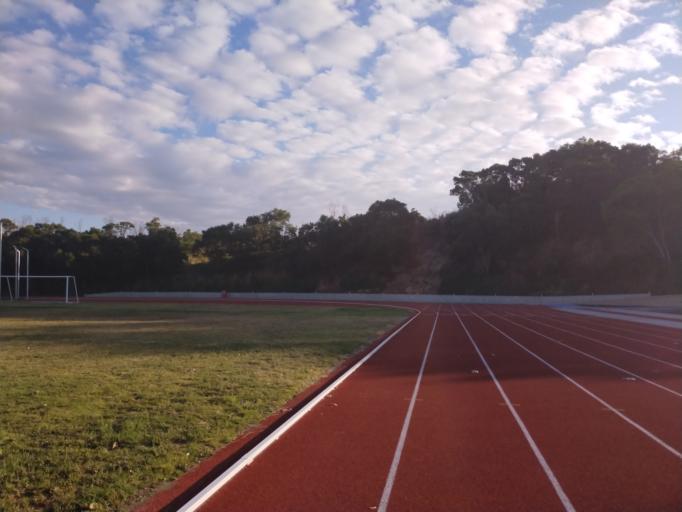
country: TW
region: Taiwan
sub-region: Changhua
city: Chang-hua
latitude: 24.1339
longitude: 120.5990
